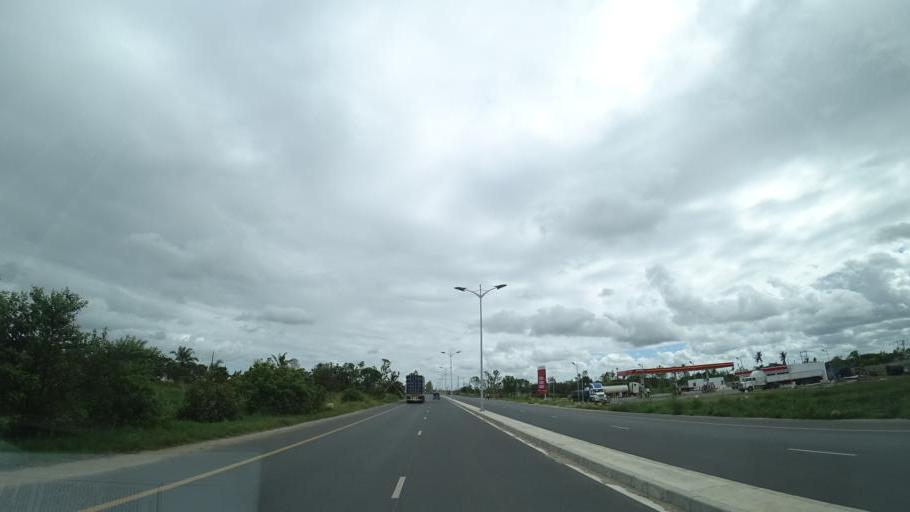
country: MZ
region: Sofala
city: Dondo
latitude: -19.7019
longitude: 34.7876
